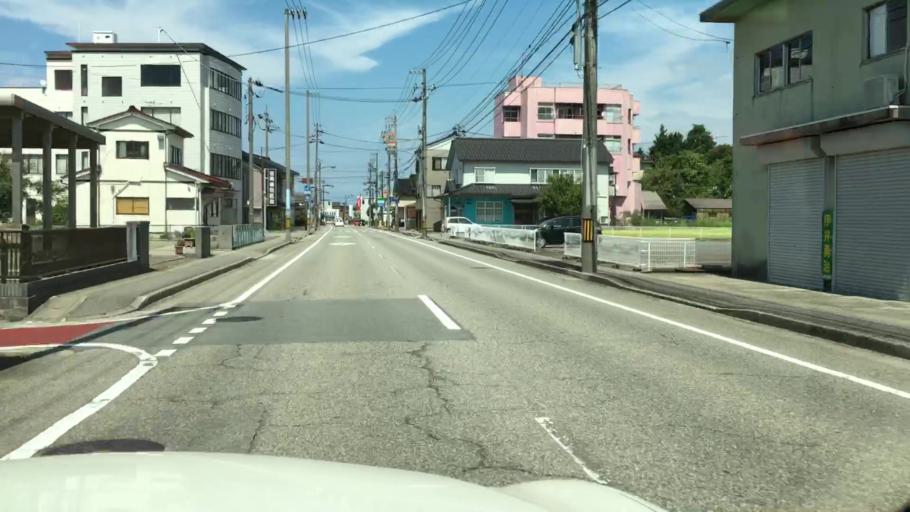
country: JP
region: Toyama
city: Kamiichi
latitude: 36.7022
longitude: 137.3579
